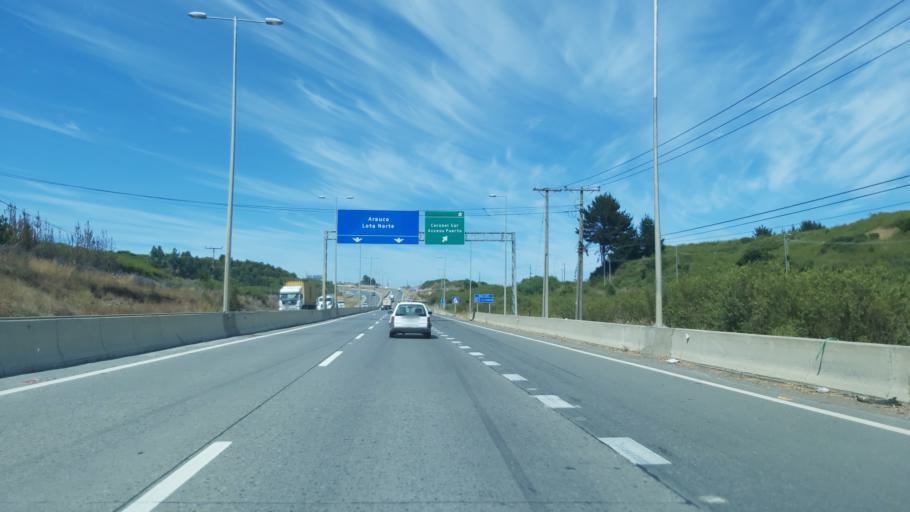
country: CL
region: Biobio
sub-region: Provincia de Concepcion
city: Coronel
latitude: -37.0430
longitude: -73.1388
